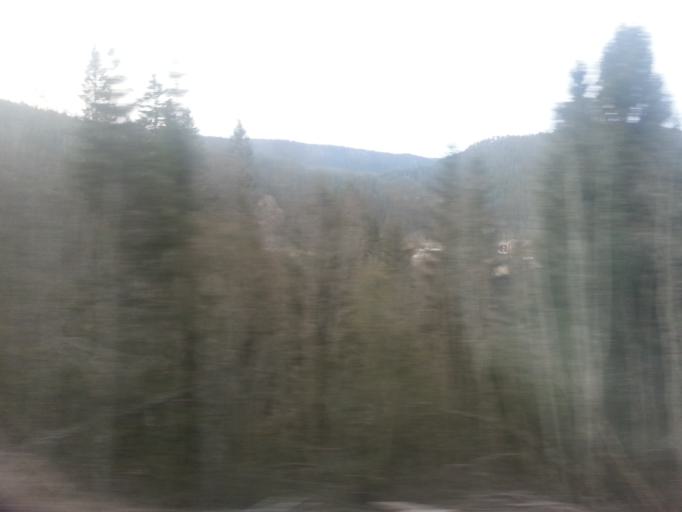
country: NO
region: Sor-Trondelag
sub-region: Midtre Gauldal
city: Storen
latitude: 63.0183
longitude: 10.2400
